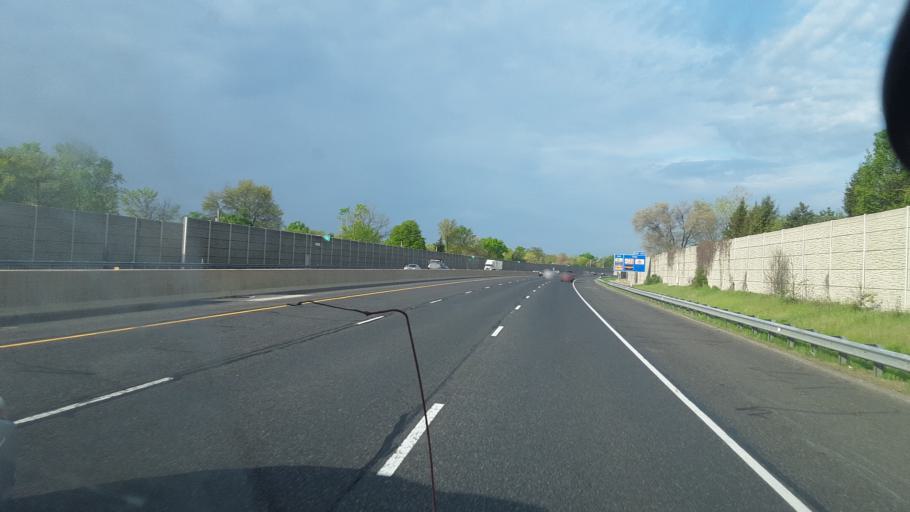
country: US
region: Indiana
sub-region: Allen County
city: Fort Wayne
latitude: 41.1466
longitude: -85.1188
